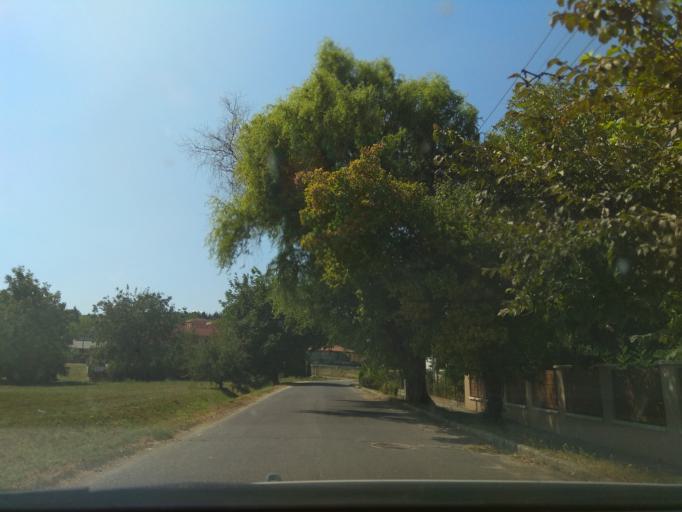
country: HU
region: Borsod-Abauj-Zemplen
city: Miskolc
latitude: 48.0640
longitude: 20.7830
